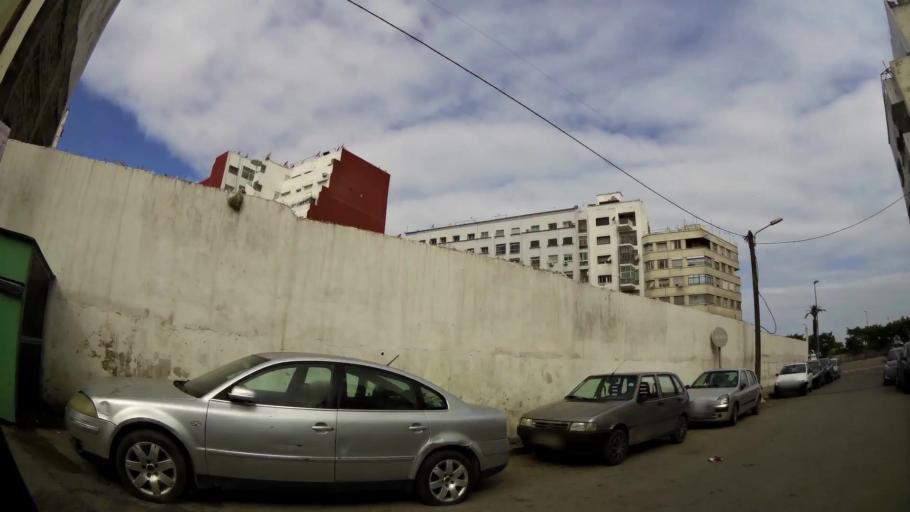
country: MA
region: Grand Casablanca
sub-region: Casablanca
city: Casablanca
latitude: 33.5966
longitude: -7.5915
